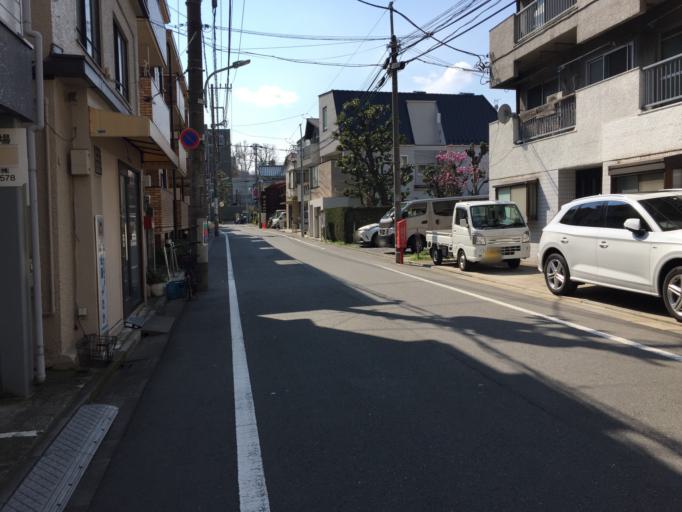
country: JP
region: Tokyo
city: Tokyo
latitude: 35.6381
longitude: 139.7035
